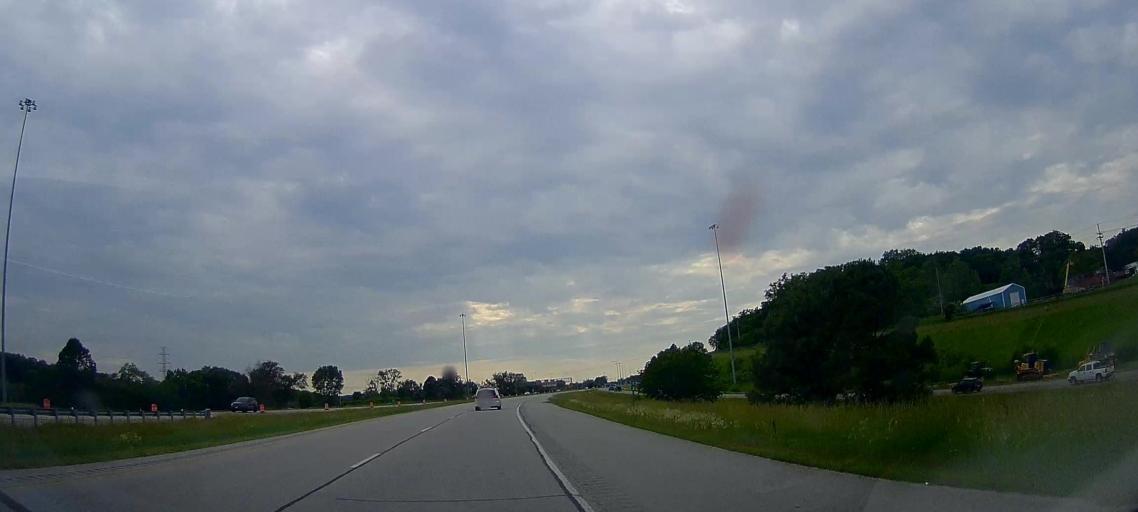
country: US
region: Iowa
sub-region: Pottawattamie County
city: Carter Lake
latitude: 41.3447
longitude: -95.9654
